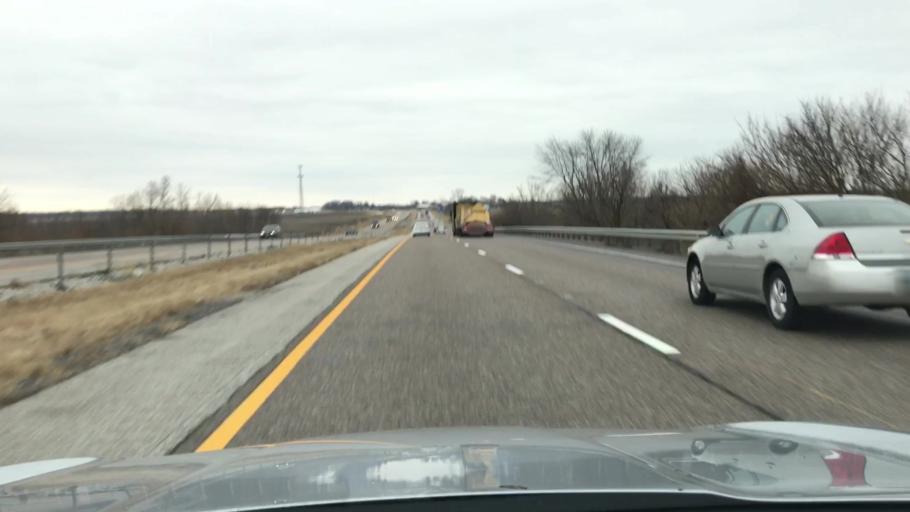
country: US
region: Illinois
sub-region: Madison County
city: Edwardsville
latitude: 38.8241
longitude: -89.8838
